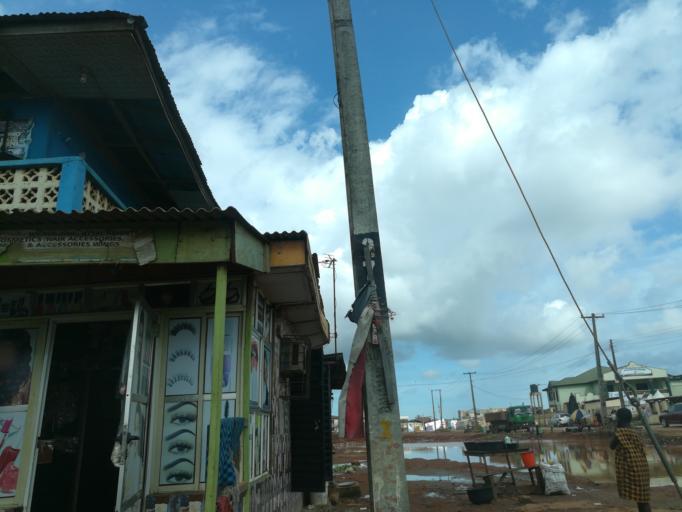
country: NG
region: Lagos
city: Ikorodu
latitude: 6.5922
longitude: 3.5166
